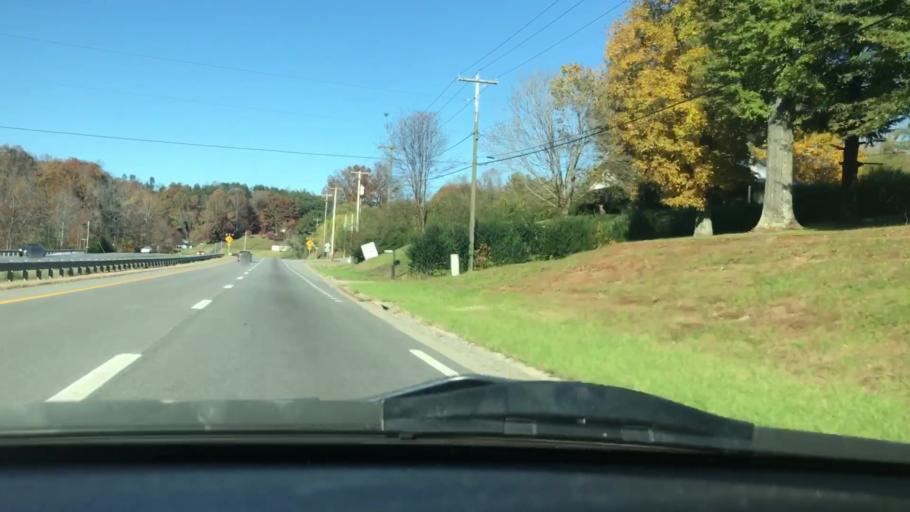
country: US
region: Virginia
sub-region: Henry County
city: Stanleytown
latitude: 36.7569
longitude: -79.9371
